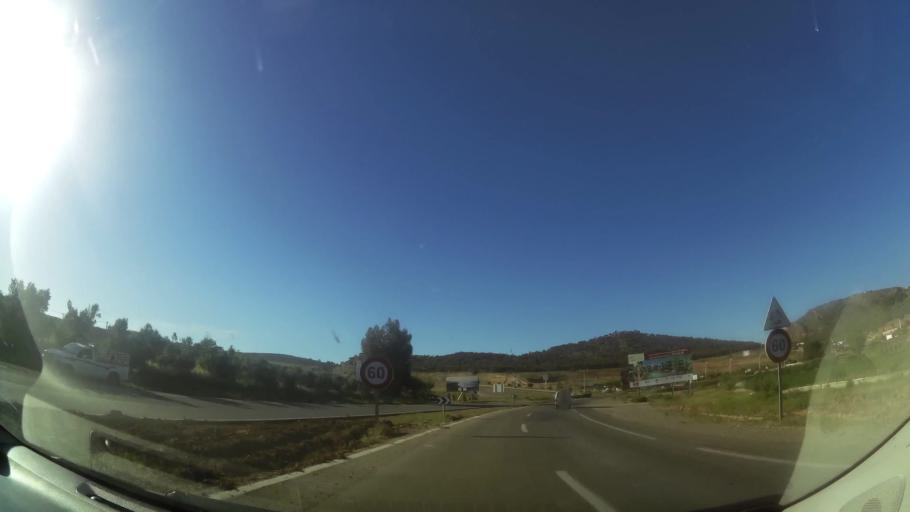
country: MA
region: Oriental
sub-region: Berkane-Taourirt
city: Madagh
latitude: 35.0490
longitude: -2.2193
